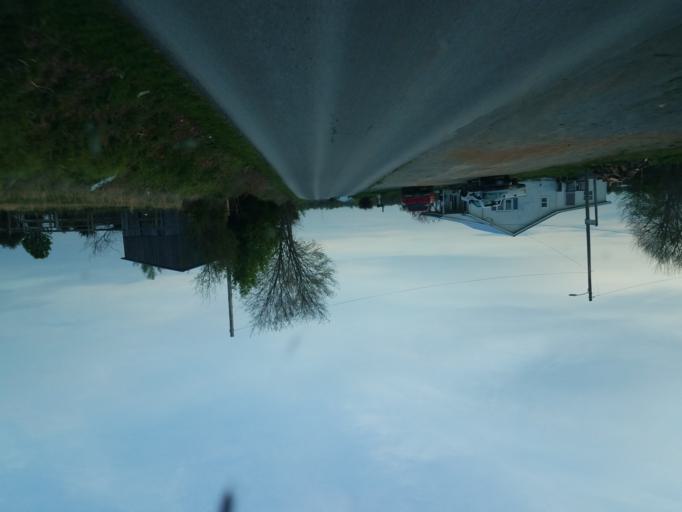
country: US
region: Kentucky
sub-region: Green County
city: Greensburg
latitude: 37.1784
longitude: -85.6848
